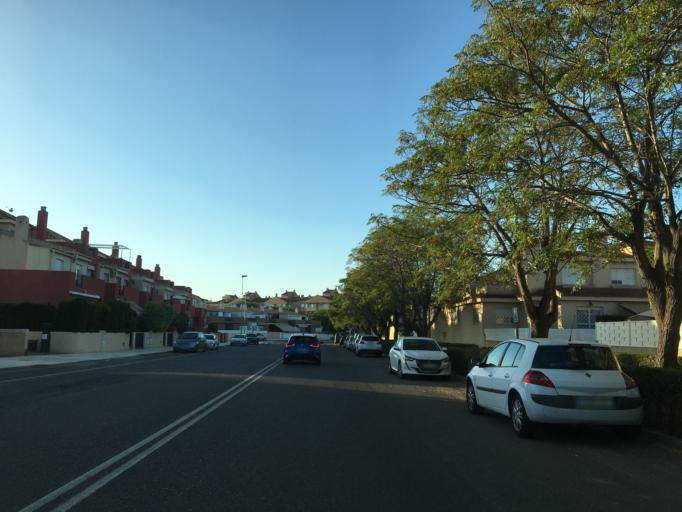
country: ES
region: Murcia
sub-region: Murcia
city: Cartagena
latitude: 37.6540
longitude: -1.0180
